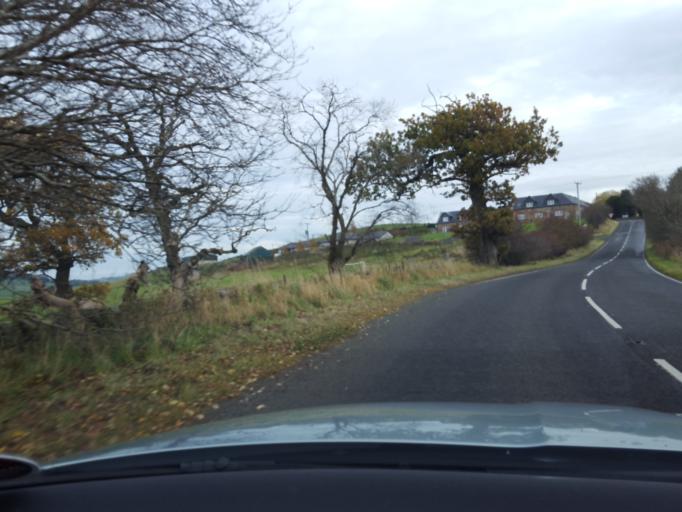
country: GB
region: Scotland
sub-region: The Scottish Borders
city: West Linton
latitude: 55.6849
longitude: -3.4019
